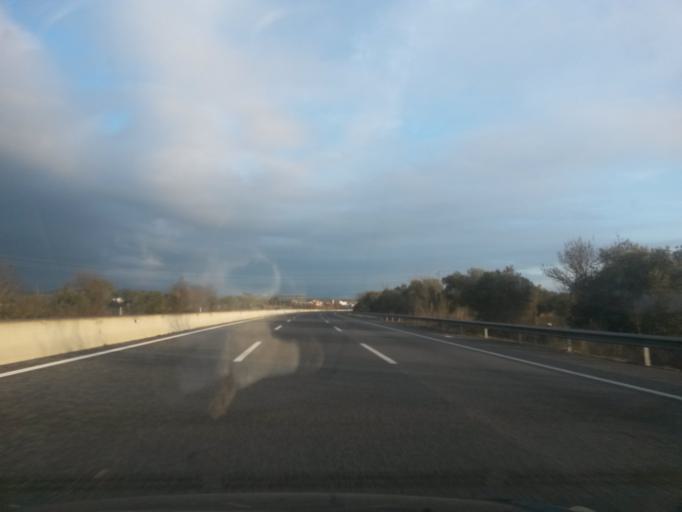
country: ES
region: Catalonia
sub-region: Provincia de Girona
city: Vilafant
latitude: 42.2366
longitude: 2.9368
